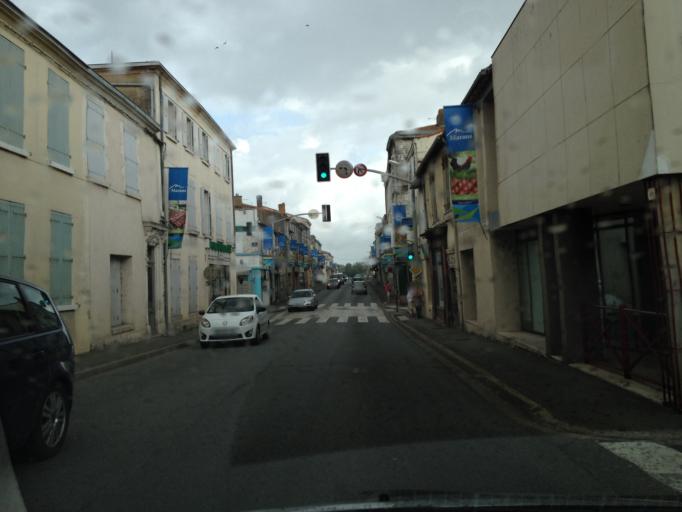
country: FR
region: Poitou-Charentes
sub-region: Departement de la Charente-Maritime
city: Marans
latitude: 46.3098
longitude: -0.9919
